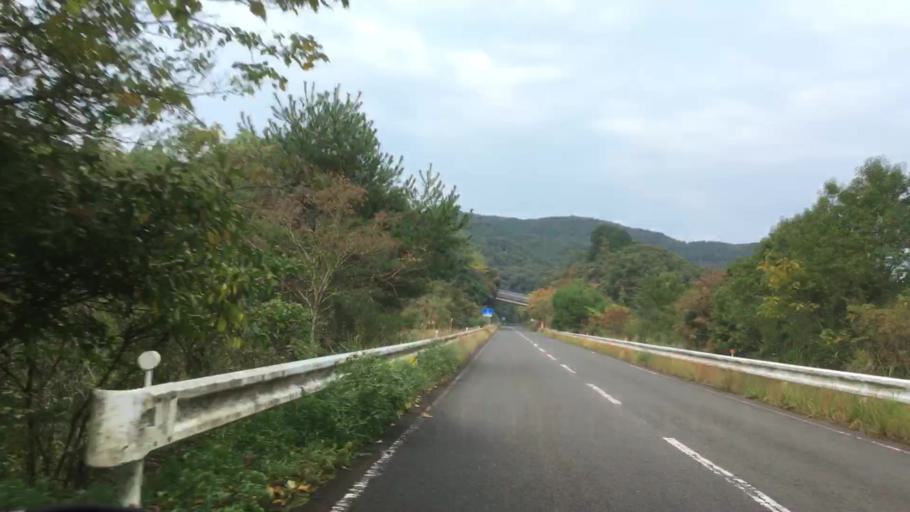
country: JP
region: Nagasaki
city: Sasebo
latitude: 32.9960
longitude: 129.7126
